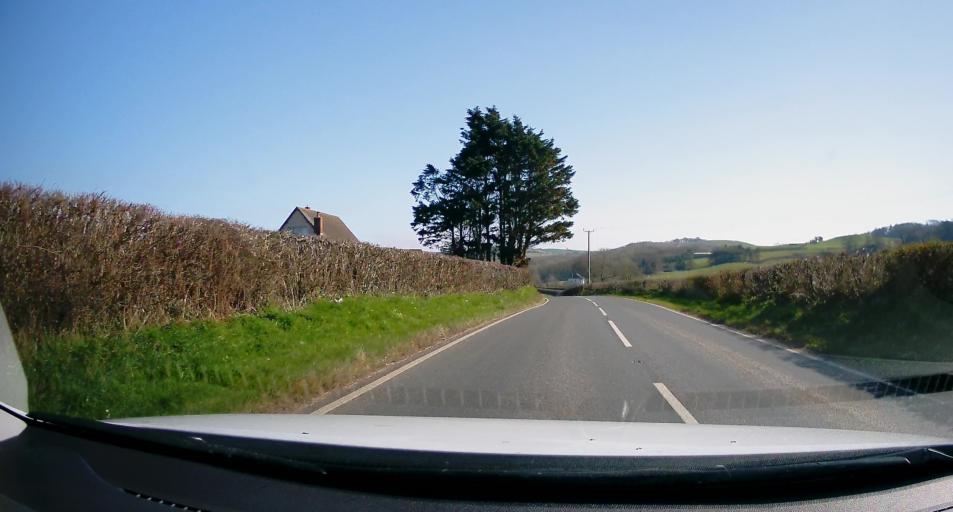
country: GB
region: Wales
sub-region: County of Ceredigion
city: Penparcau
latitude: 52.3716
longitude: -4.0699
